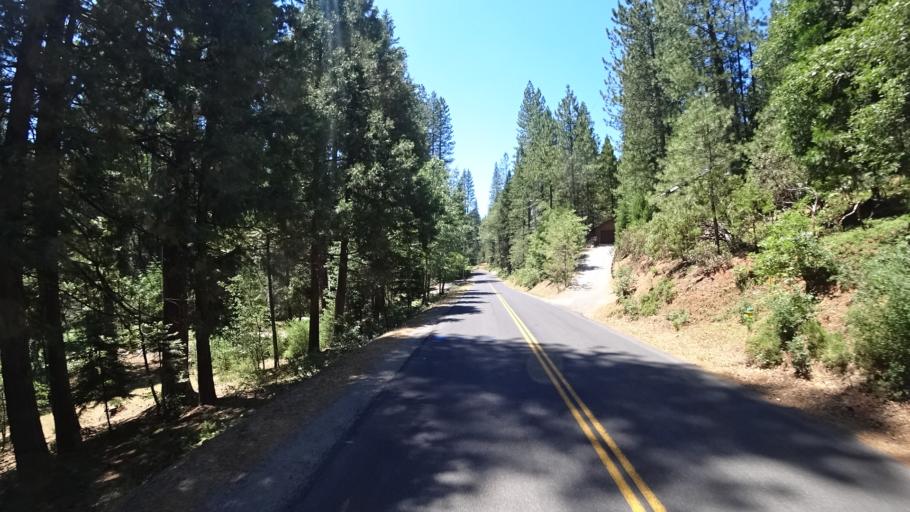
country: US
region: California
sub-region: Calaveras County
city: Arnold
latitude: 38.2350
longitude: -120.3441
